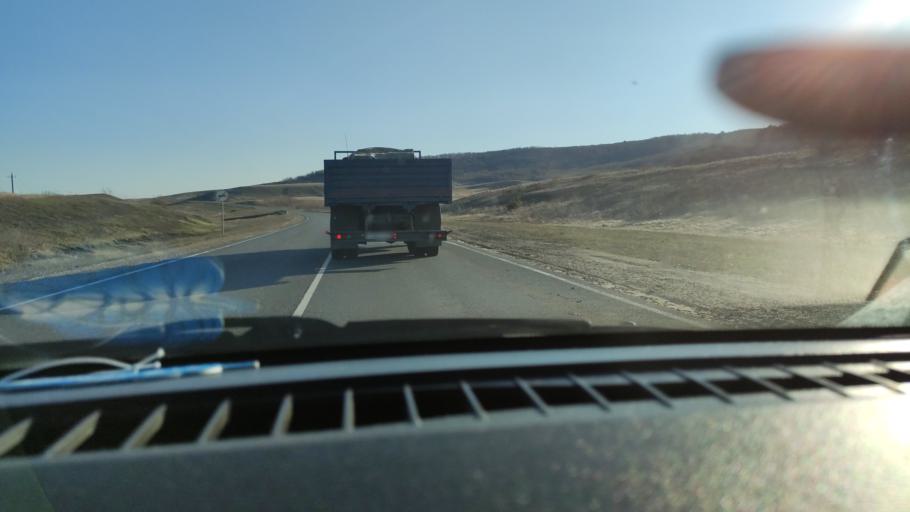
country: RU
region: Saratov
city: Alekseyevka
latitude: 52.3355
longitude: 47.9293
